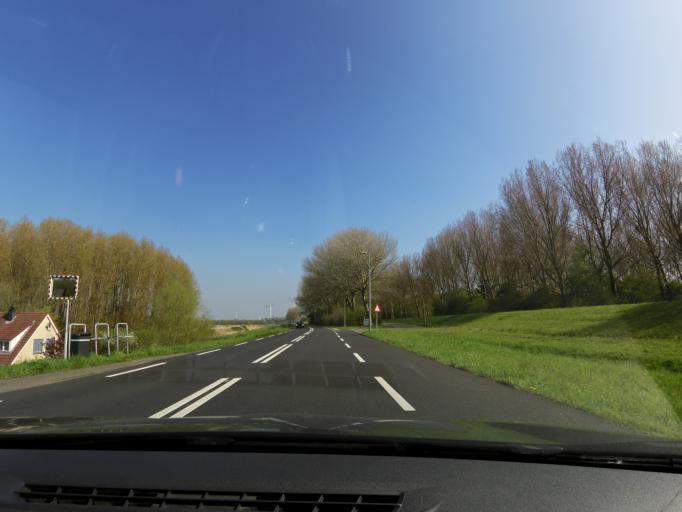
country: NL
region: South Holland
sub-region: Gemeente Maassluis
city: Maassluis
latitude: 51.9072
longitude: 4.2795
